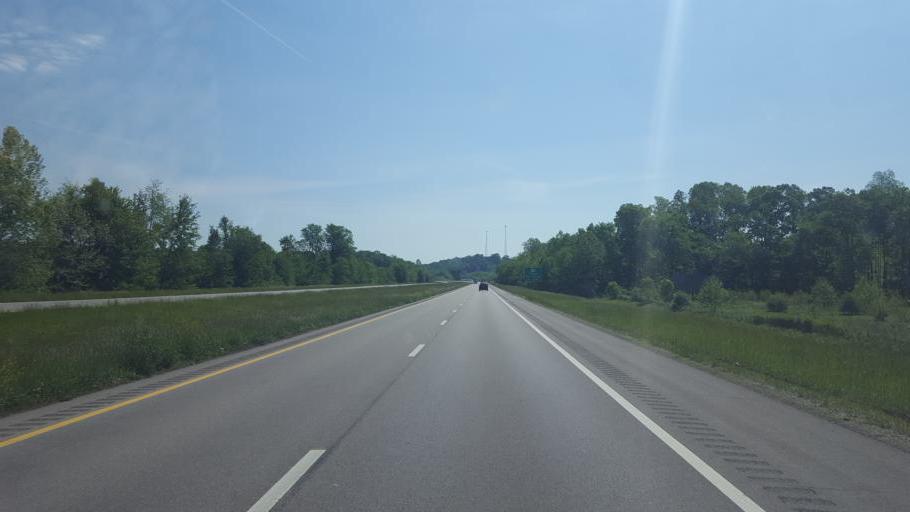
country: US
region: Ohio
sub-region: Jackson County
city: Oak Hill
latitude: 38.8867
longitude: -82.3994
